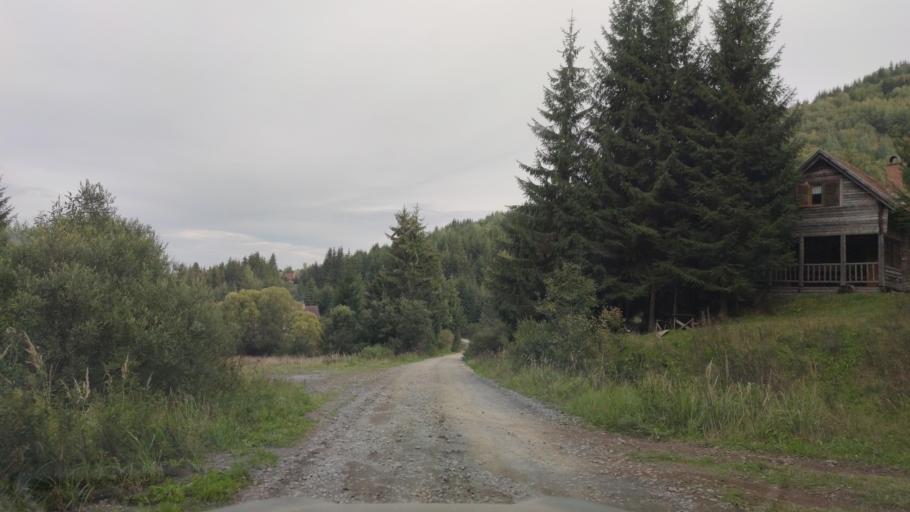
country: RO
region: Harghita
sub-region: Comuna Remetea
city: Remetea
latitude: 46.8121
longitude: 25.3609
